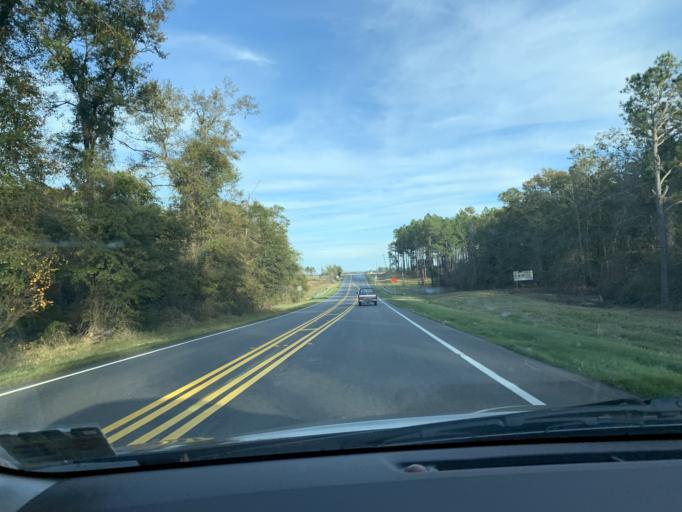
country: US
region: Georgia
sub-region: Irwin County
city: Ocilla
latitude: 31.5938
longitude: -83.1914
